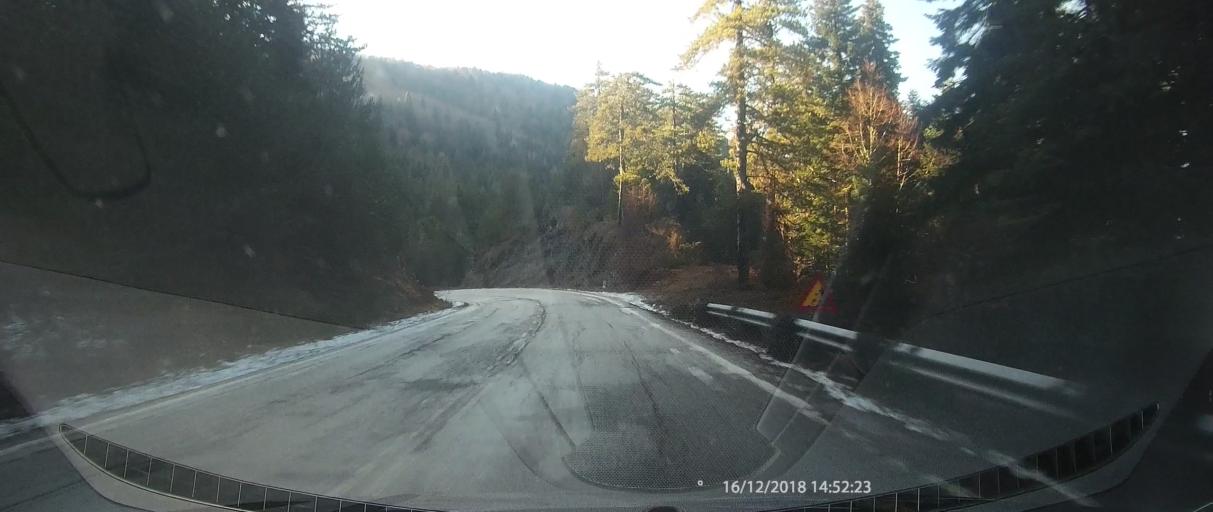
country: GR
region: West Macedonia
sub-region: Nomos Kastorias
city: Nestorio
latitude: 40.2050
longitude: 21.0626
